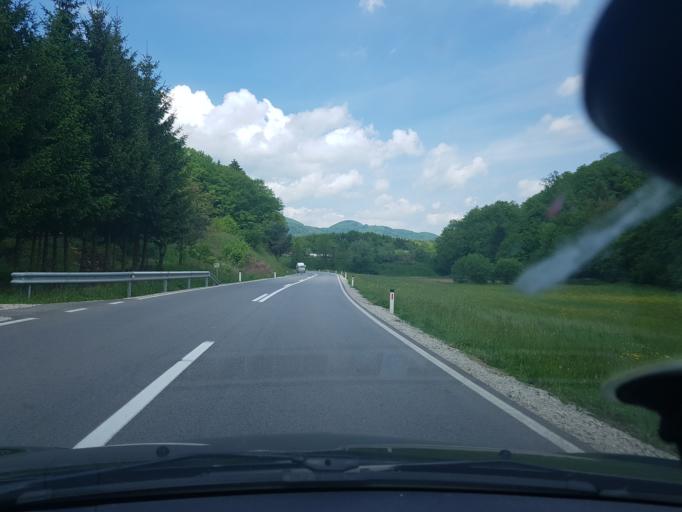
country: SI
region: Rogatec
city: Rogatec
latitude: 46.2323
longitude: 15.6730
